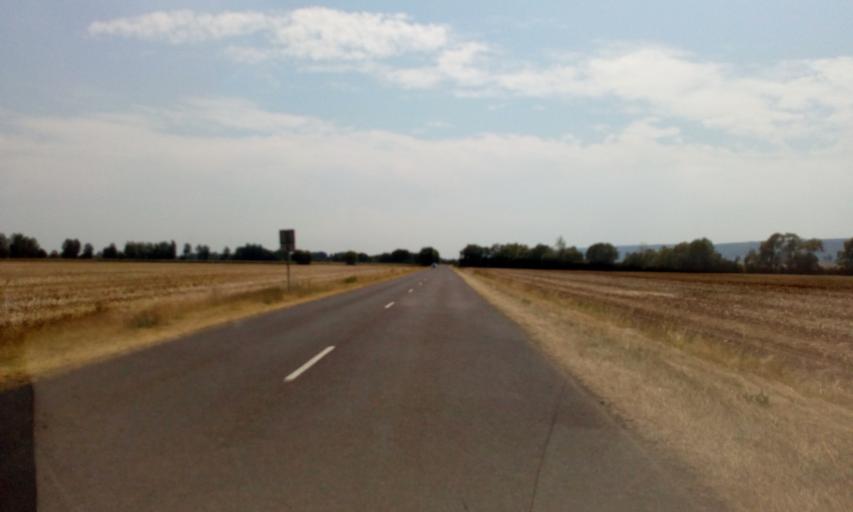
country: FR
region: Lorraine
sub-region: Departement de la Meuse
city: Etain
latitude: 49.0883
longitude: 5.6303
